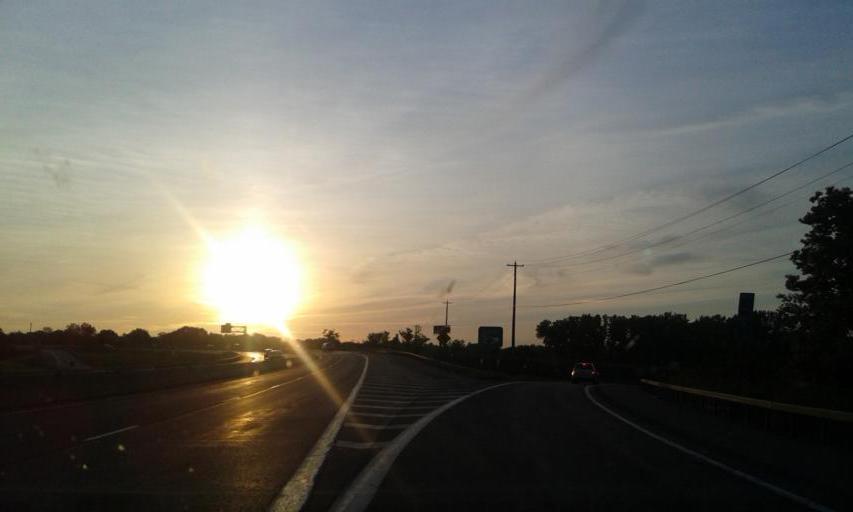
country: US
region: New York
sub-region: Onondaga County
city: Seneca Knolls
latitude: 43.1119
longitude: -76.2654
